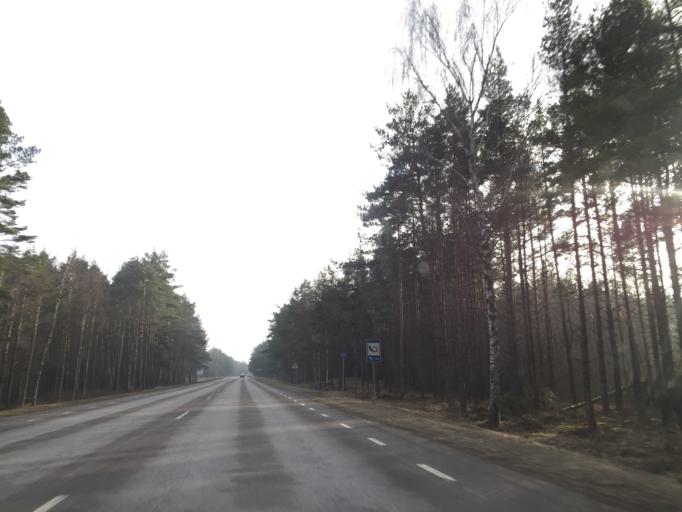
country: EE
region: Saare
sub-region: Kuressaare linn
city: Kuressaare
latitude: 58.4128
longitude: 22.7805
